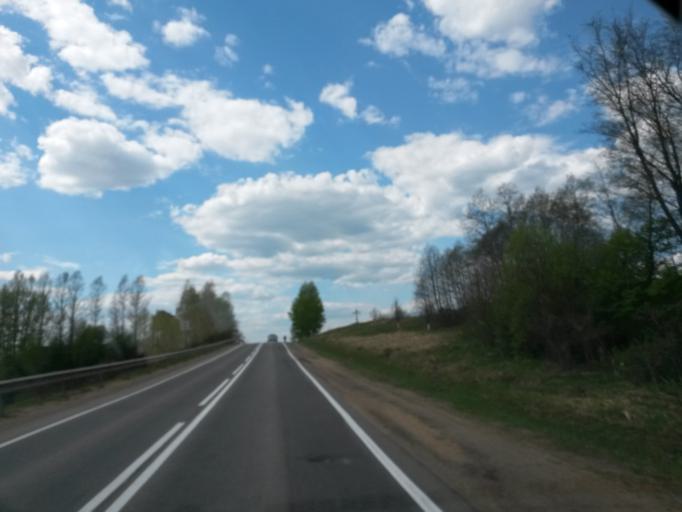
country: RU
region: Jaroslavl
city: Bol'shoye Selo
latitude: 57.7204
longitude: 38.9622
